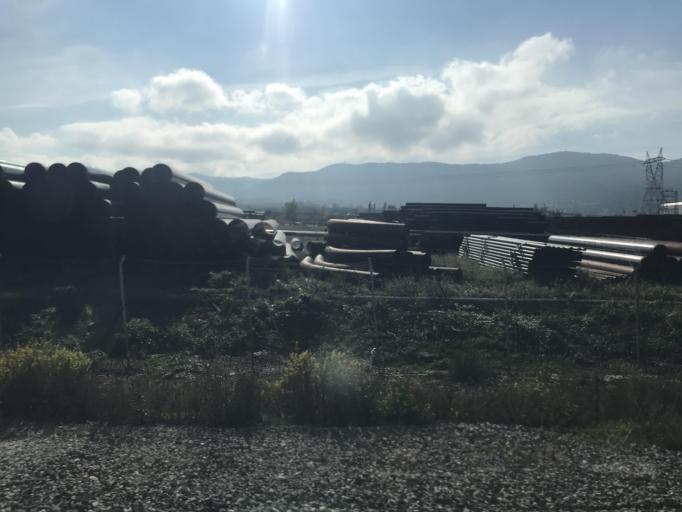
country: ES
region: Basque Country
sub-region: Provincia de Alava
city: Gasteiz / Vitoria
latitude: 42.8235
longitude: -2.7817
